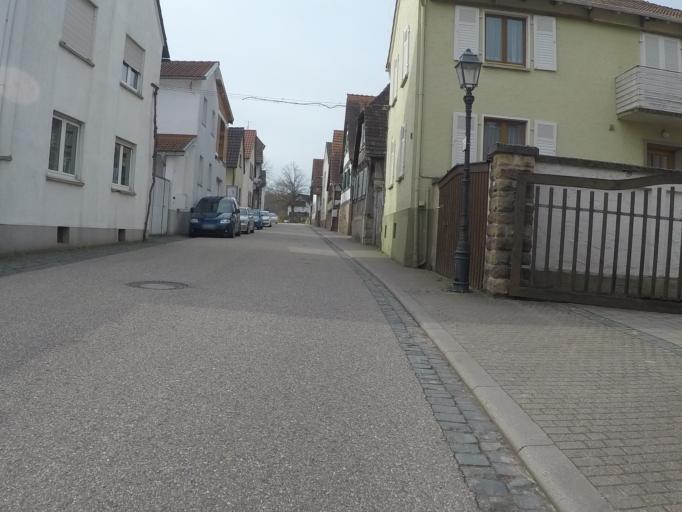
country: DE
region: Rheinland-Pfalz
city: Heuchelheim-Klingen
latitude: 49.1398
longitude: 8.0573
